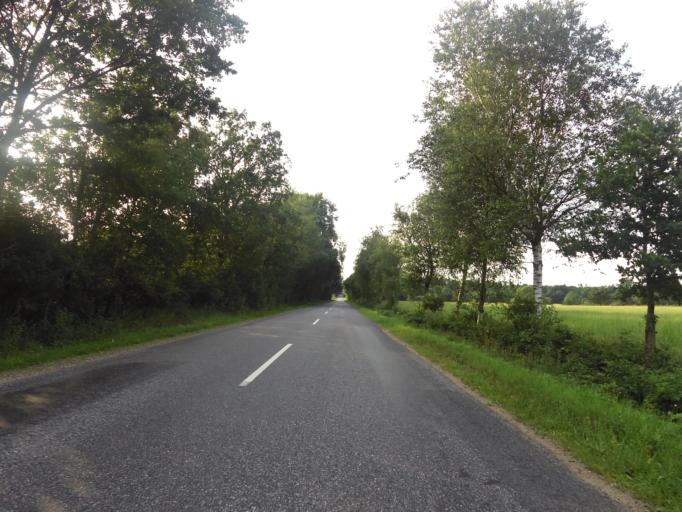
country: DK
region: South Denmark
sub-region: Tonder Kommune
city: Sherrebek
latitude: 55.1954
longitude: 8.8944
